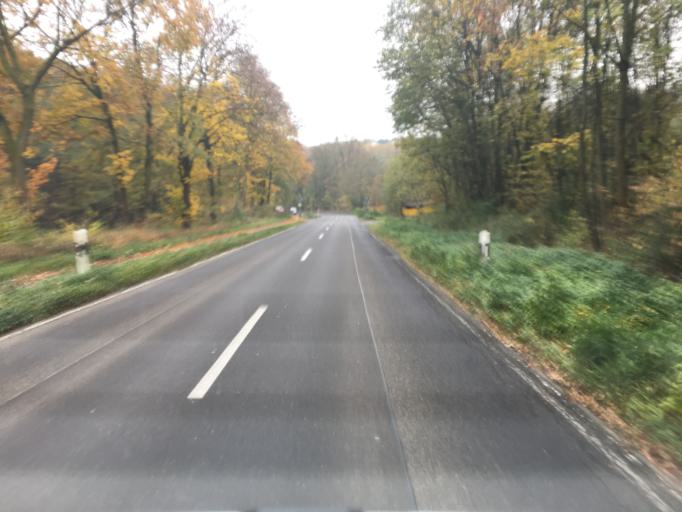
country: DE
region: North Rhine-Westphalia
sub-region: Regierungsbezirk Dusseldorf
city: Velbert
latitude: 51.3229
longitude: 7.0851
